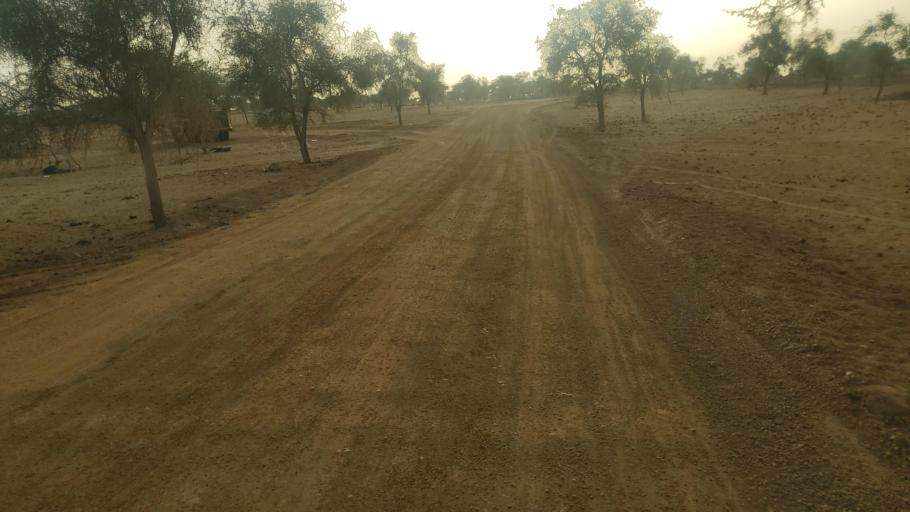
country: SN
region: Louga
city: Dara
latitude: 15.3665
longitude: -15.5650
